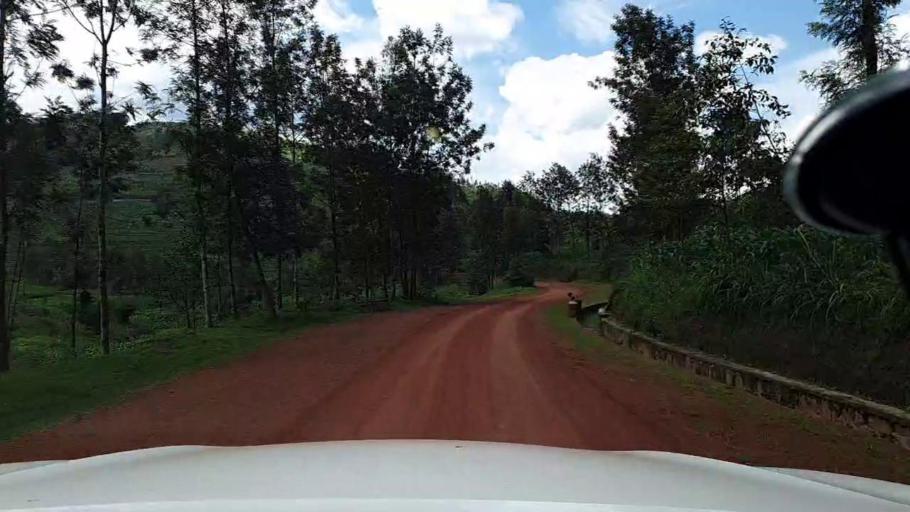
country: RW
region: Northern Province
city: Byumba
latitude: -1.7055
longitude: 29.8422
